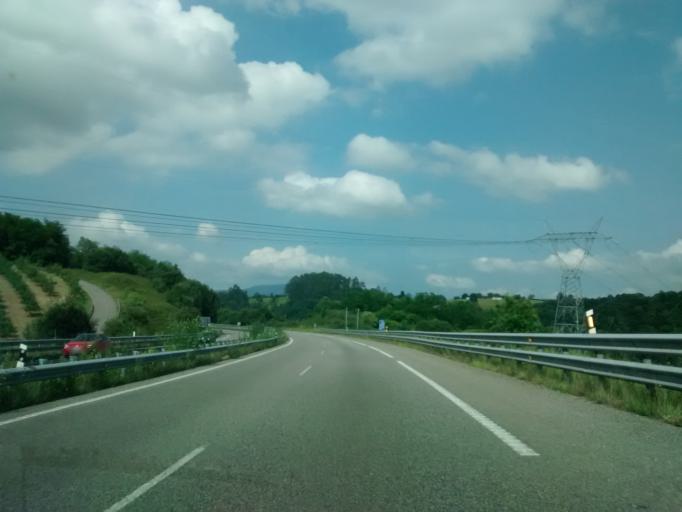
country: ES
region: Asturias
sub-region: Province of Asturias
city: Pola de Siero
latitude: 43.3474
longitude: -5.6834
